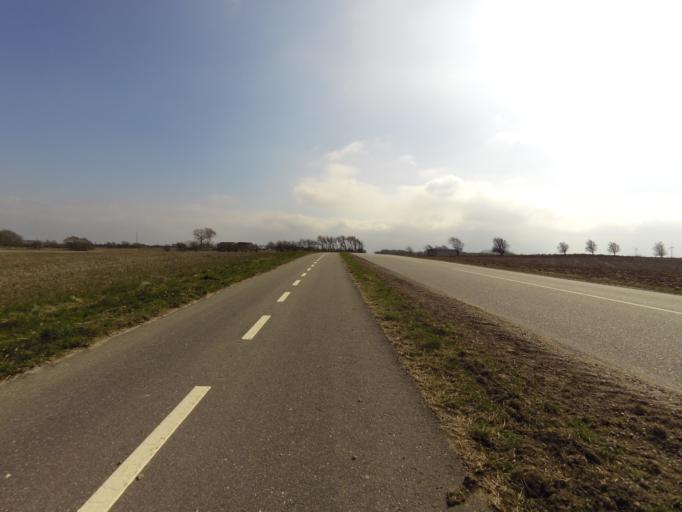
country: DK
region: Central Jutland
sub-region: Struer Kommune
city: Struer
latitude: 56.4455
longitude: 8.6250
